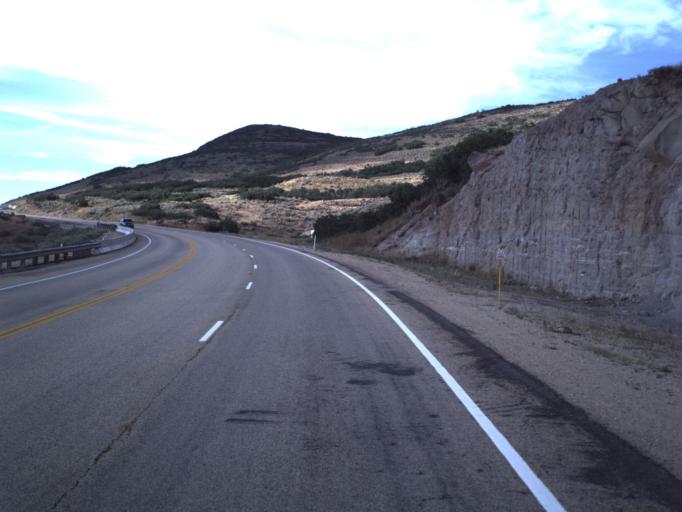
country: US
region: Utah
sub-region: Wasatch County
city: Heber
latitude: 40.5786
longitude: -111.4199
